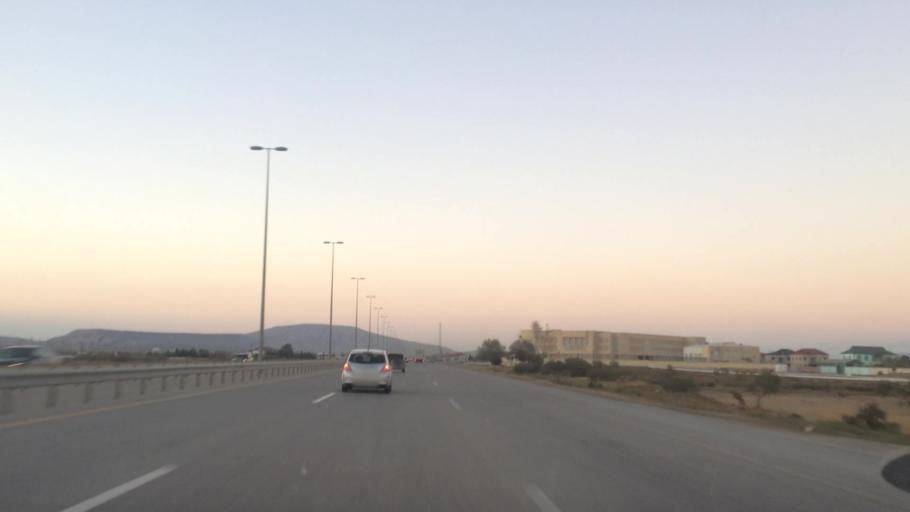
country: AZ
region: Baki
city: Qobustan
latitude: 40.0502
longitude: 49.4178
